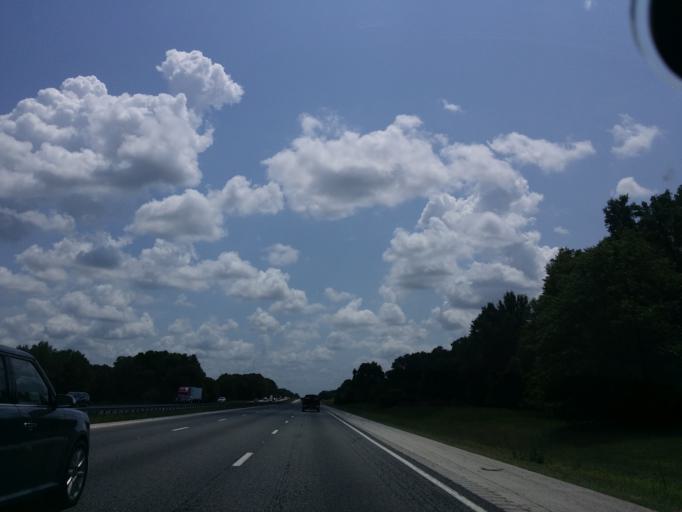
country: US
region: Florida
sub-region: Marion County
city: Ocala
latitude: 29.2914
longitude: -82.2021
